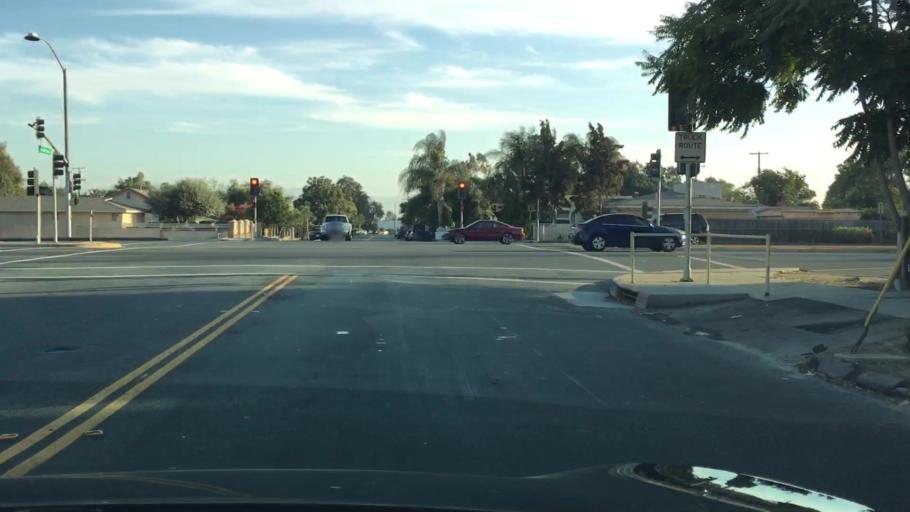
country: US
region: California
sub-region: San Bernardino County
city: Ontario
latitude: 34.0554
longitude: -117.6367
